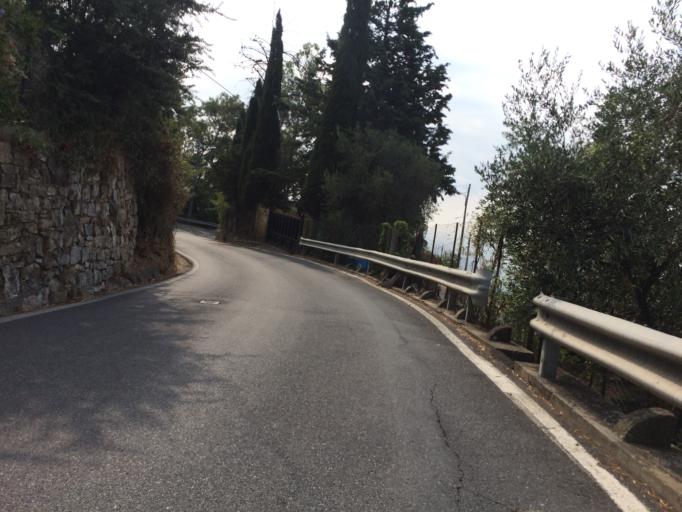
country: IT
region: Liguria
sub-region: Provincia di Imperia
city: San Remo
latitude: 43.8421
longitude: 7.7472
